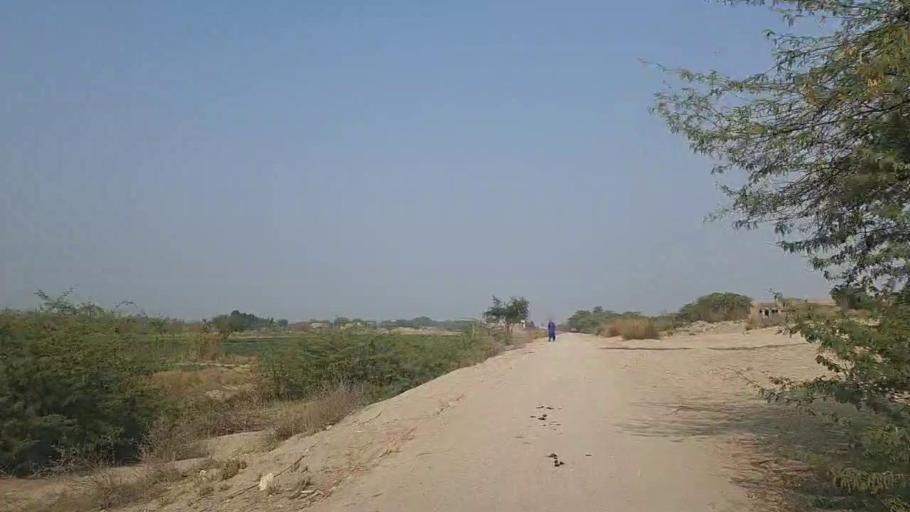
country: PK
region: Sindh
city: Daur
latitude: 26.4390
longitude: 68.4428
